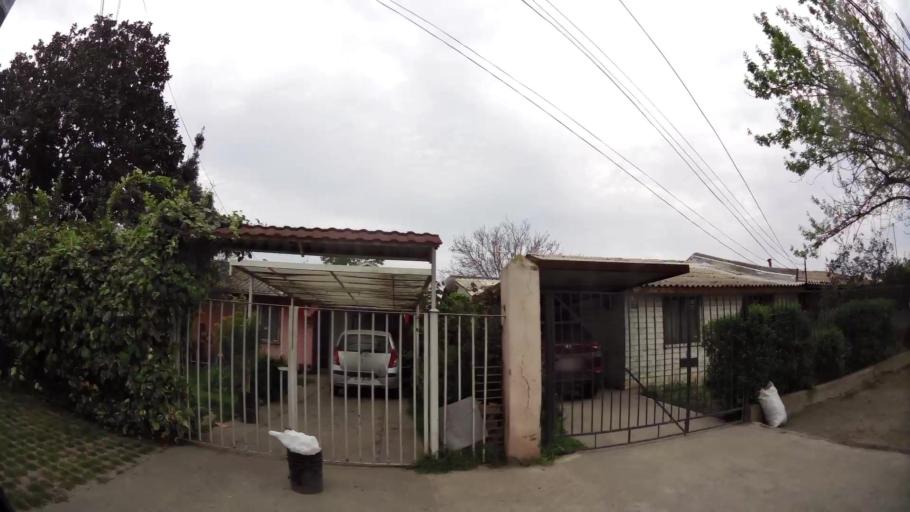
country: CL
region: Santiago Metropolitan
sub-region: Provincia de Santiago
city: Lo Prado
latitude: -33.4999
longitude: -70.7656
